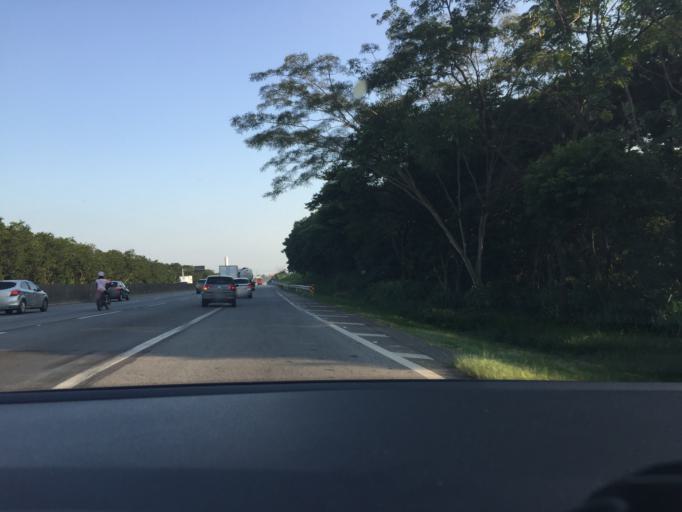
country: BR
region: Sao Paulo
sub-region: Louveira
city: Louveira
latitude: -23.0986
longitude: -46.9675
